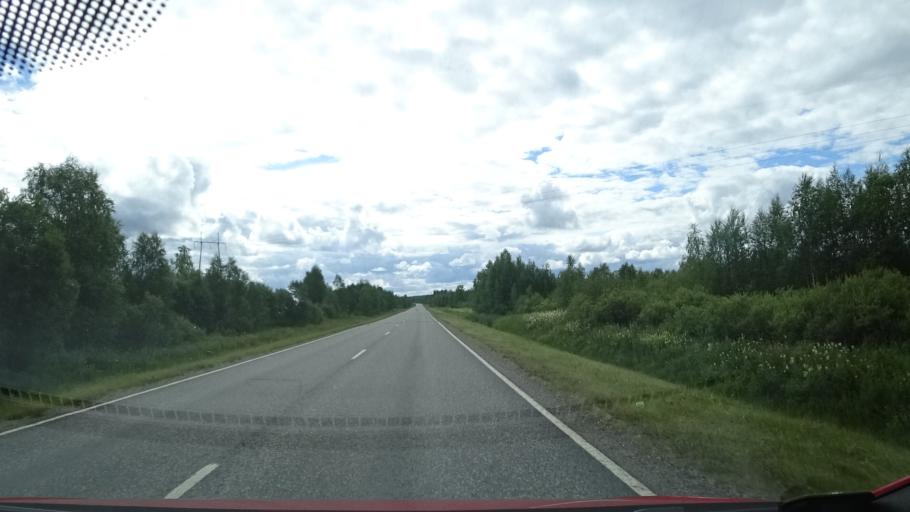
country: FI
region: Lapland
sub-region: Tunturi-Lappi
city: Kittilae
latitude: 67.5463
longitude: 24.9159
